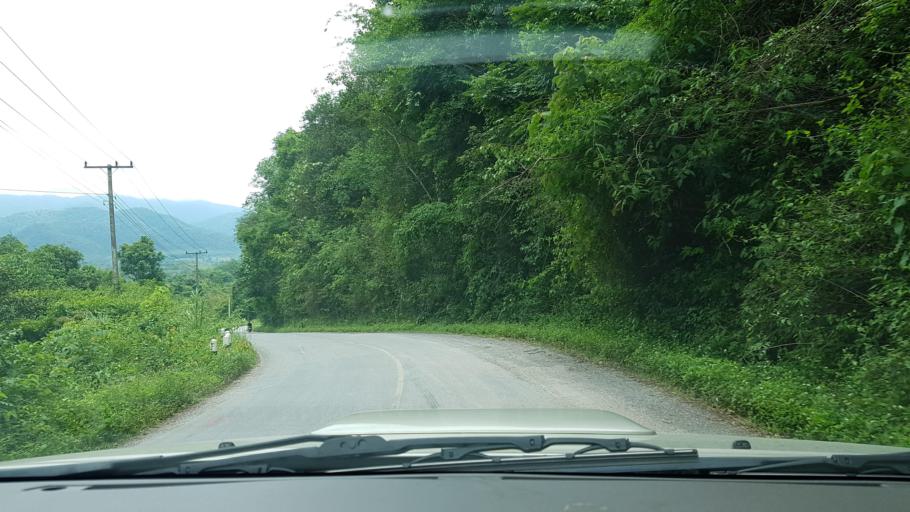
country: LA
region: Oudomxai
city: Muang Xay
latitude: 20.7242
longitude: 102.0188
